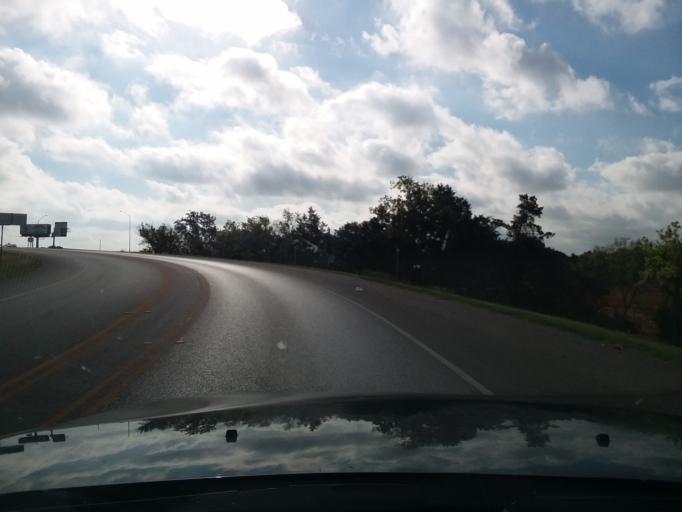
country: US
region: Texas
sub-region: Denton County
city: Hickory Creek
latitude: 33.1213
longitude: -97.0358
